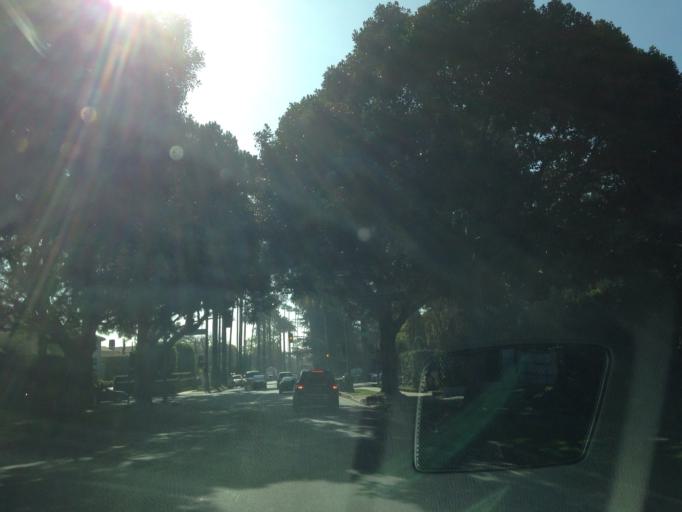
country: US
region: California
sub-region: Los Angeles County
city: Beverly Hills
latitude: 34.0863
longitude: -118.4130
